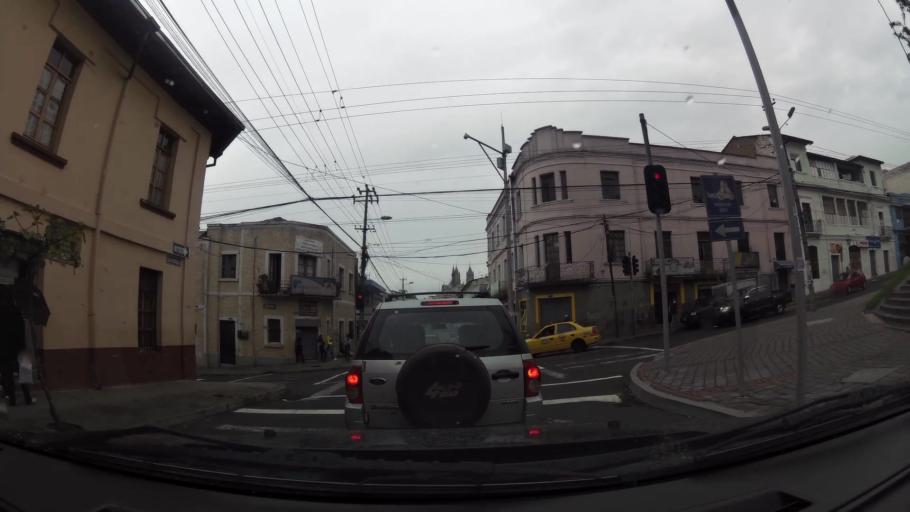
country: EC
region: Pichincha
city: Quito
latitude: -0.2083
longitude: -78.5049
